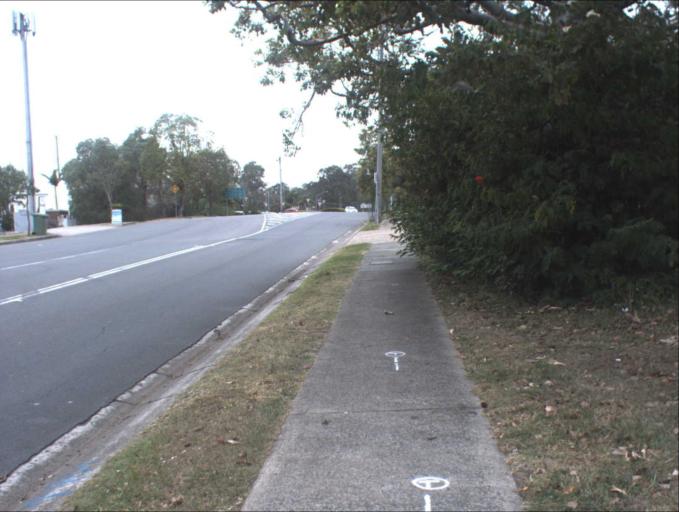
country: AU
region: Queensland
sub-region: Logan
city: Slacks Creek
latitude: -27.6637
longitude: 153.1707
